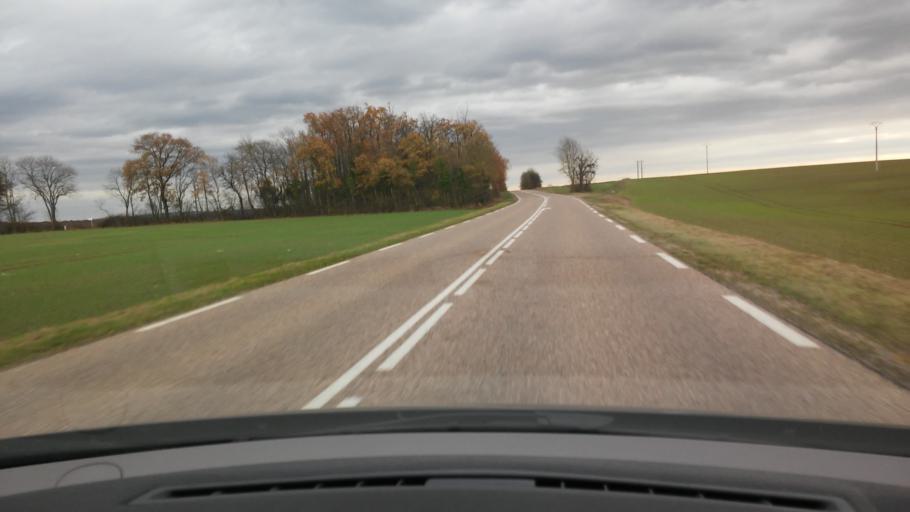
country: FR
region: Lorraine
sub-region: Departement de la Moselle
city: Retonfey
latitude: 49.1476
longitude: 6.3477
